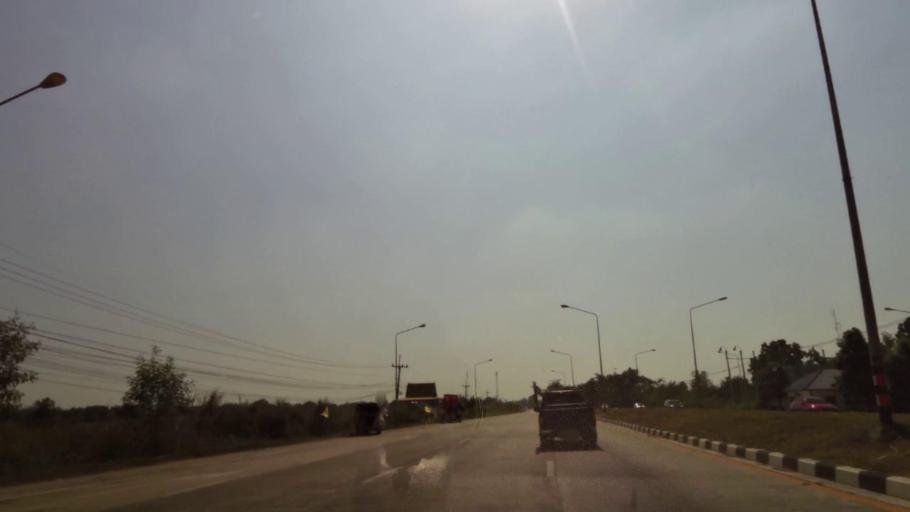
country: TH
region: Phichit
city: Wachira Barami
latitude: 16.3539
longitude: 100.1288
